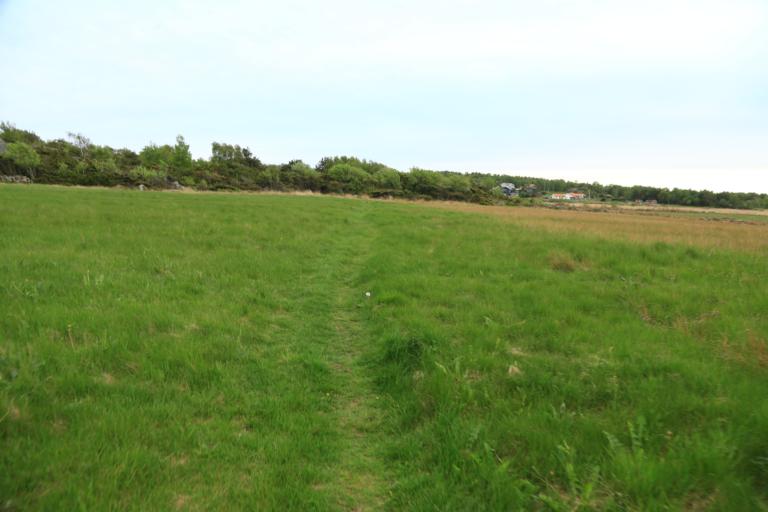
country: SE
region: Halland
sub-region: Varbergs Kommun
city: Varberg
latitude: 57.1552
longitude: 12.2298
